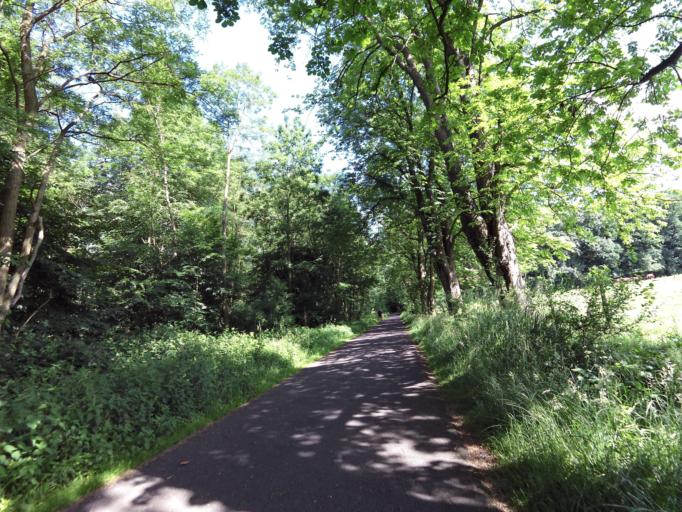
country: DE
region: North Rhine-Westphalia
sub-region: Regierungsbezirk Koln
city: Bonn
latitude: 50.6848
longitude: 7.1123
